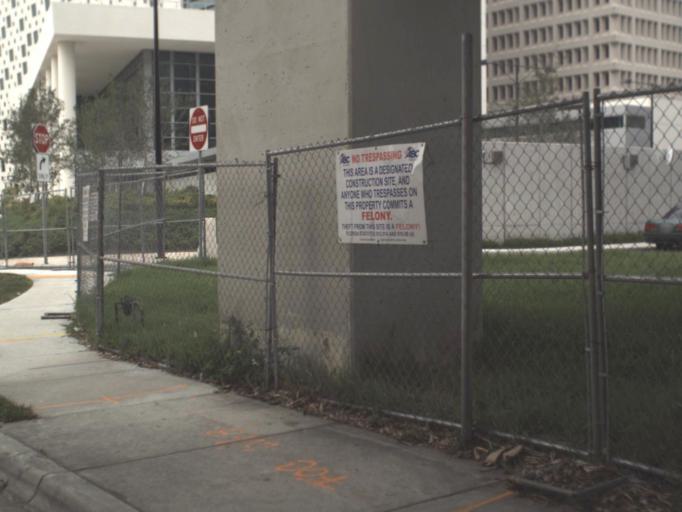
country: US
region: Florida
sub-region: Miami-Dade County
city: Miami
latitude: 25.7770
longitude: -80.1961
